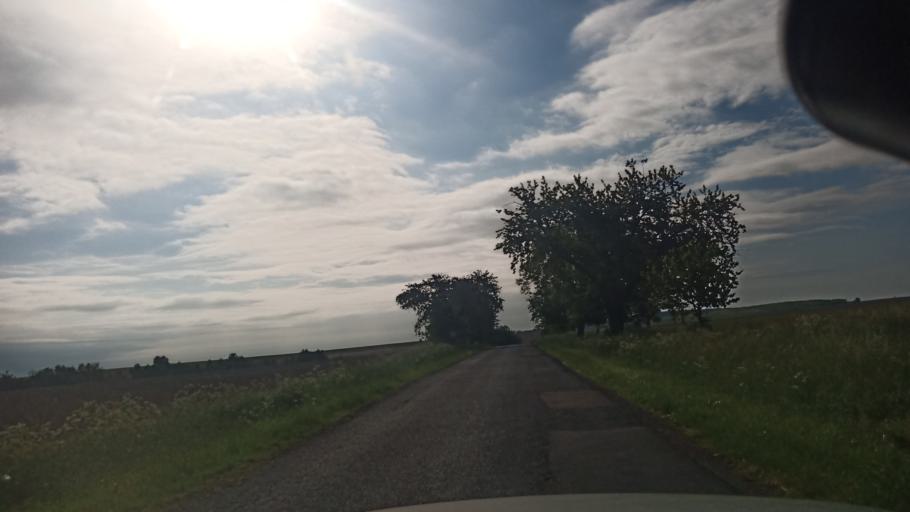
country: HU
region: Zala
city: Pacsa
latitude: 46.7083
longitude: 17.0437
